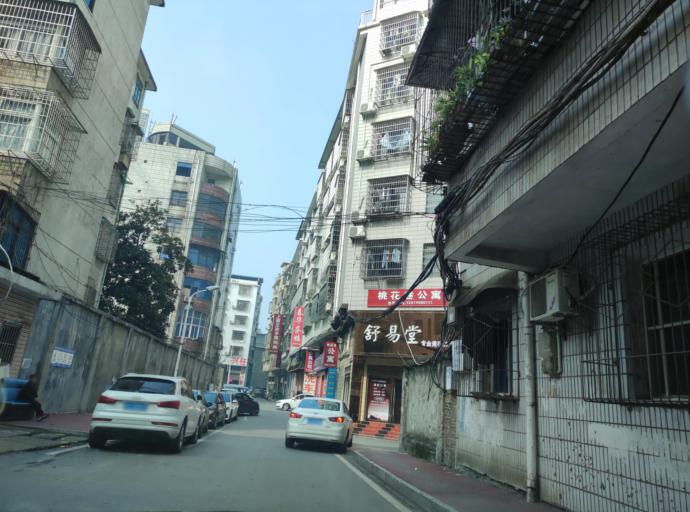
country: CN
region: Jiangxi Sheng
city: Pingxiang
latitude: 27.6452
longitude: 113.8414
